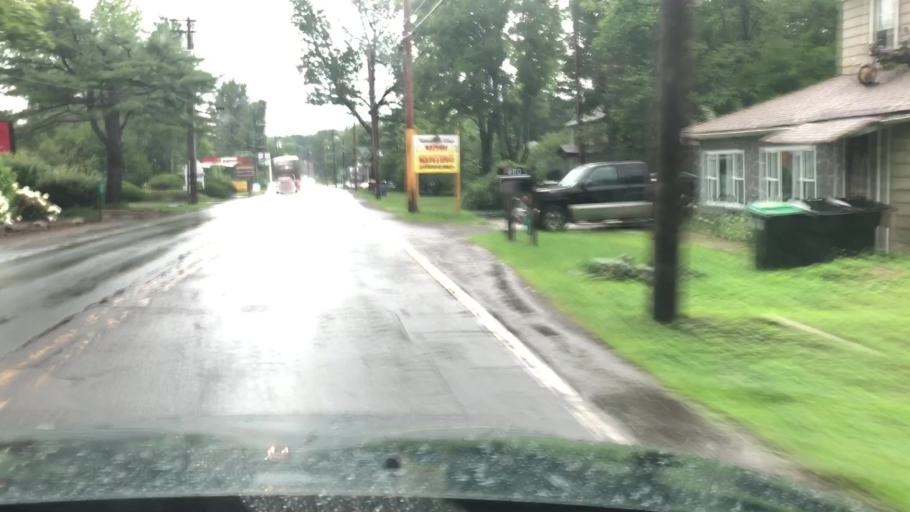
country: US
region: Pennsylvania
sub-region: Monroe County
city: Mountainhome
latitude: 41.1768
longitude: -75.2699
